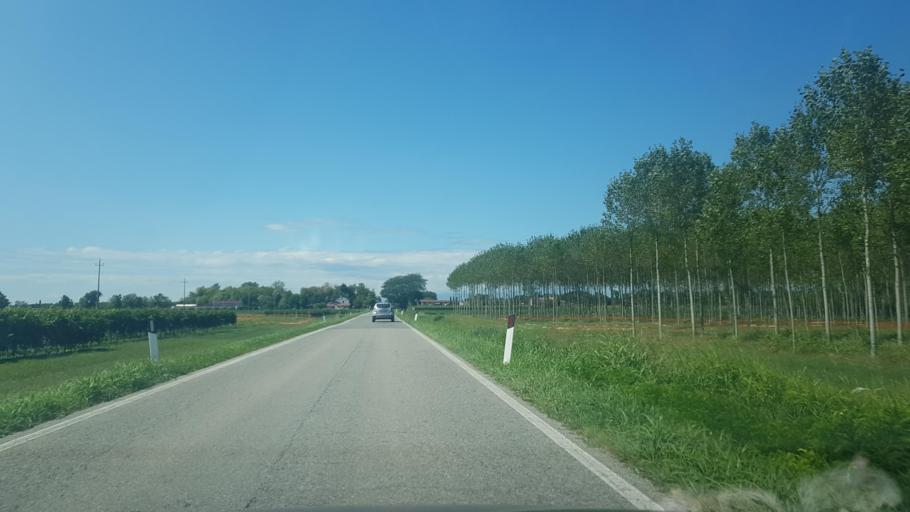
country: IT
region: Friuli Venezia Giulia
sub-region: Provincia di Udine
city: Castions di Strada
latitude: 45.8654
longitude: 13.1594
